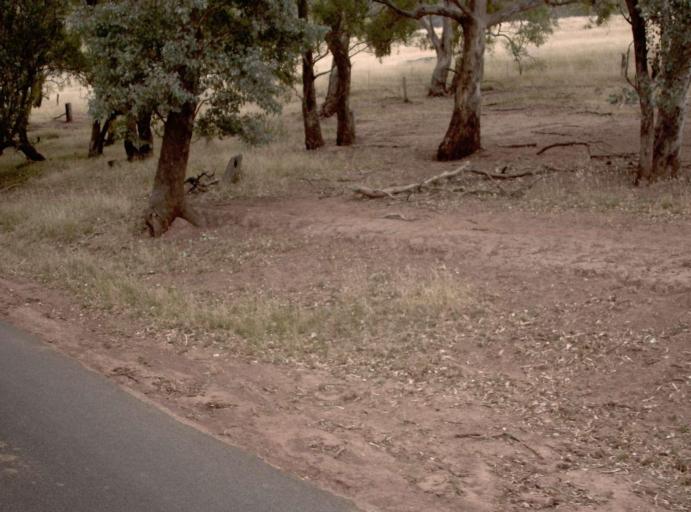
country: AU
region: Victoria
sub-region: Wellington
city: Heyfield
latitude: -37.6620
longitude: 146.6460
